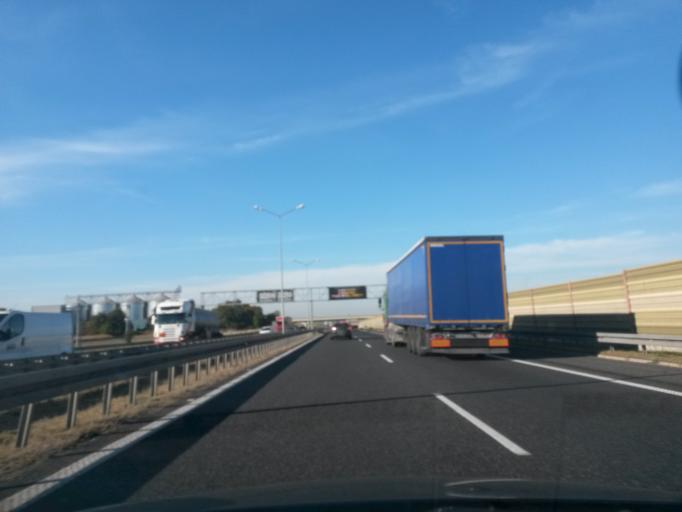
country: PL
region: Lower Silesian Voivodeship
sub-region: Powiat wroclawski
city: Zorawina
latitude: 50.9771
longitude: 17.0616
